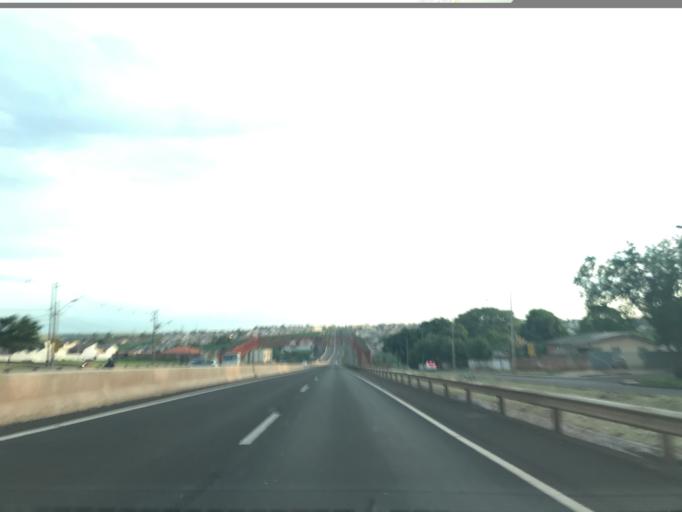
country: BR
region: Parana
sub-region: Maringa
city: Maringa
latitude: -23.3920
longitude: -51.9709
